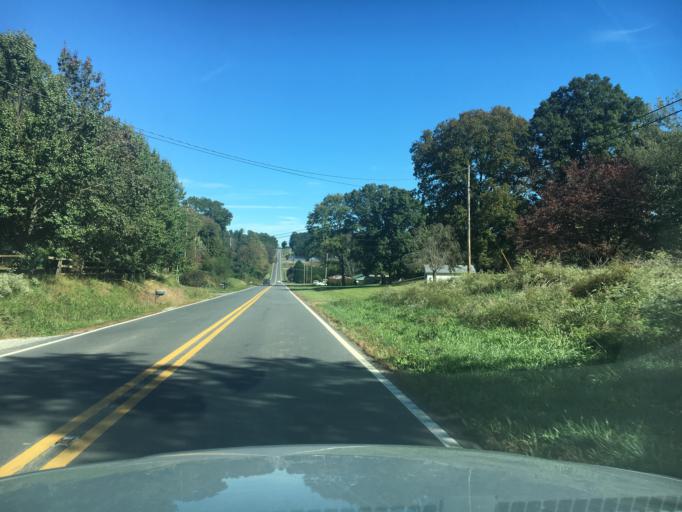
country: US
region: North Carolina
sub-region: Burke County
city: Salem
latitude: 35.6724
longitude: -81.7378
